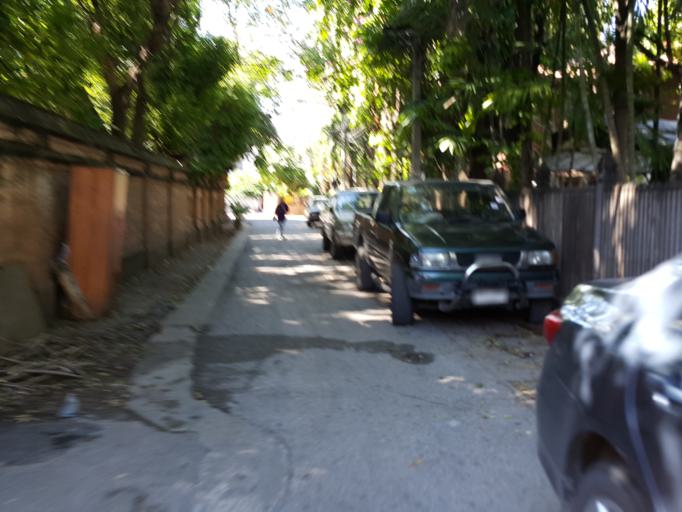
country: TH
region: Chiang Mai
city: Chiang Mai
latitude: 18.7822
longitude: 98.9877
